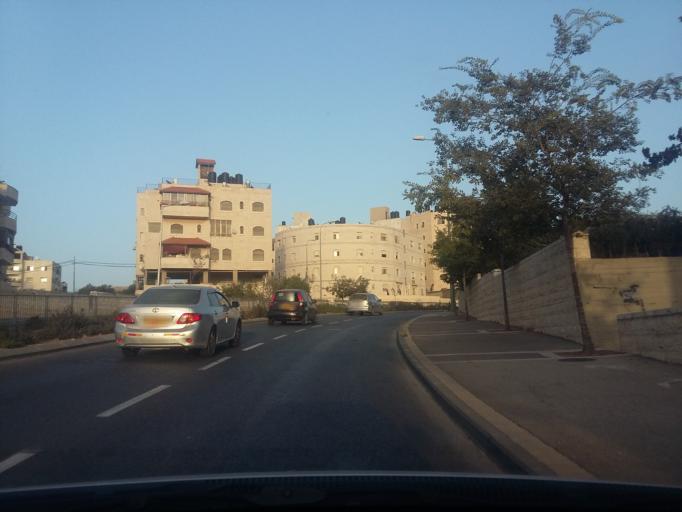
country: PS
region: West Bank
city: Ar Ram wa Dahiyat al Barid
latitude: 31.8293
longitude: 35.2312
